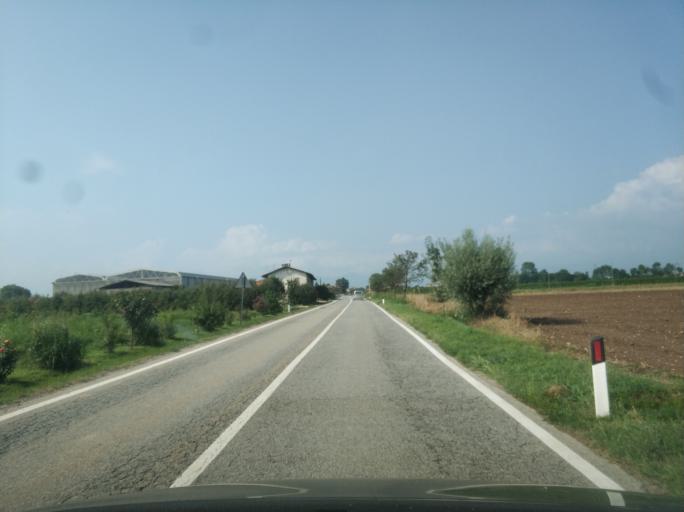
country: IT
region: Piedmont
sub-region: Provincia di Cuneo
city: Tarantasca
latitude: 44.4938
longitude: 7.5584
